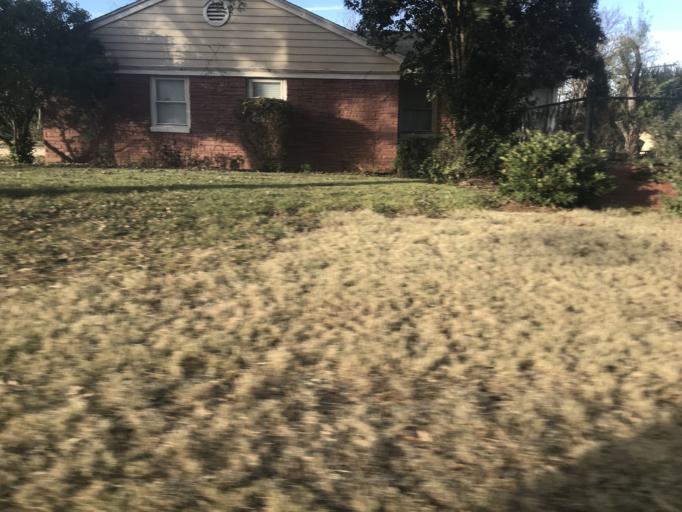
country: US
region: Texas
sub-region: Taylor County
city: Abilene
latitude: 32.4324
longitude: -99.7712
